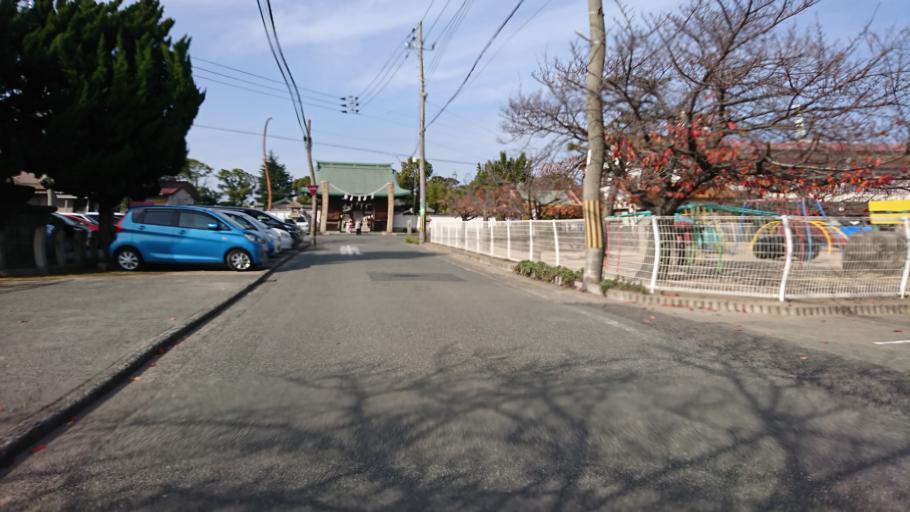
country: JP
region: Hyogo
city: Kakogawacho-honmachi
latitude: 34.7433
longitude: 134.8250
